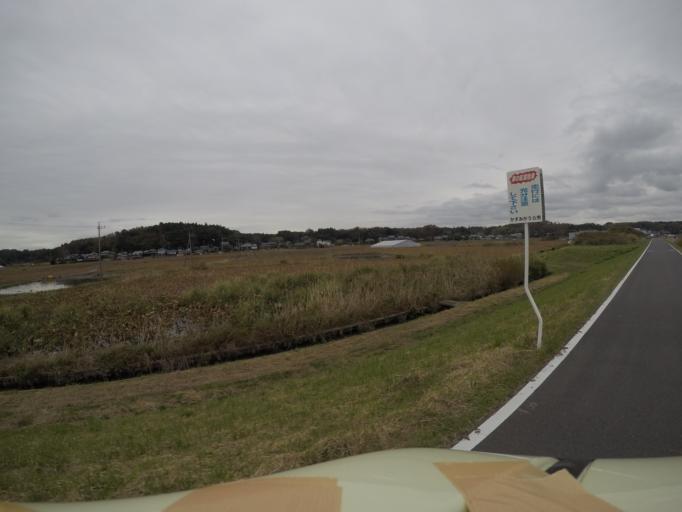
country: JP
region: Ibaraki
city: Ami
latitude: 36.0676
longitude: 140.3025
